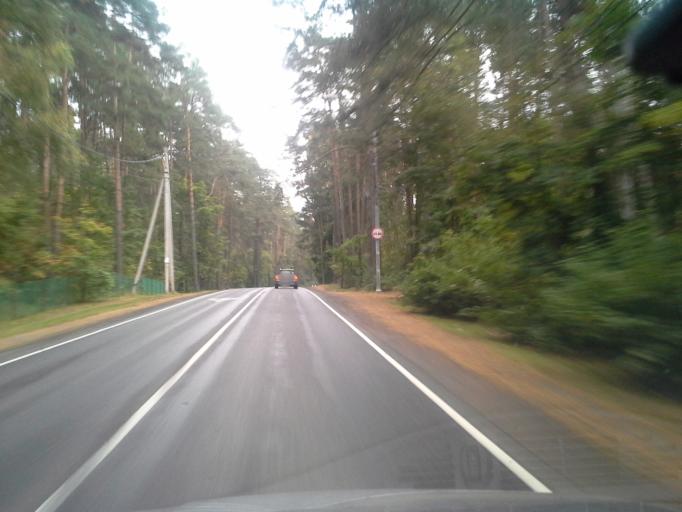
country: RU
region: Moskovskaya
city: Nikolina Gora
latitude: 55.7337
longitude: 37.0413
